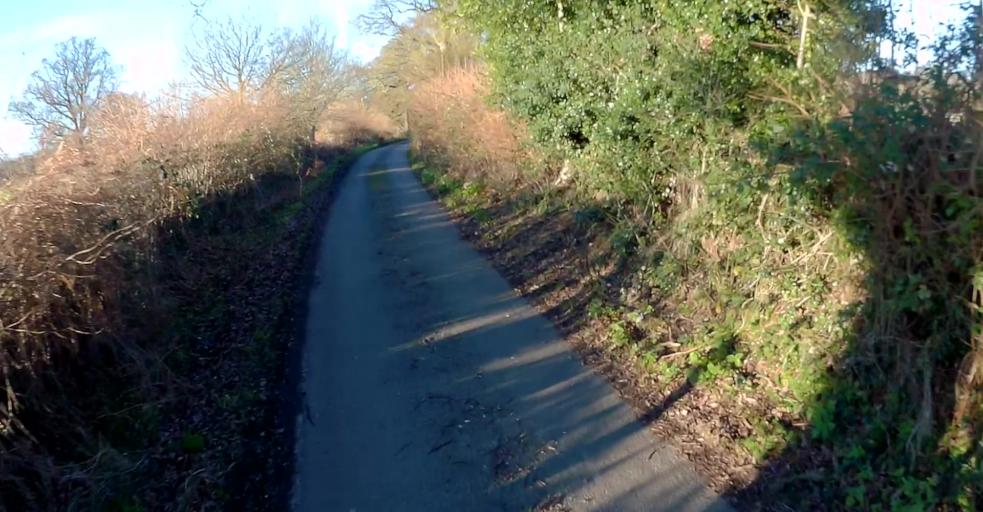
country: GB
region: England
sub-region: Hampshire
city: Hook
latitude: 51.3067
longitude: -0.9949
